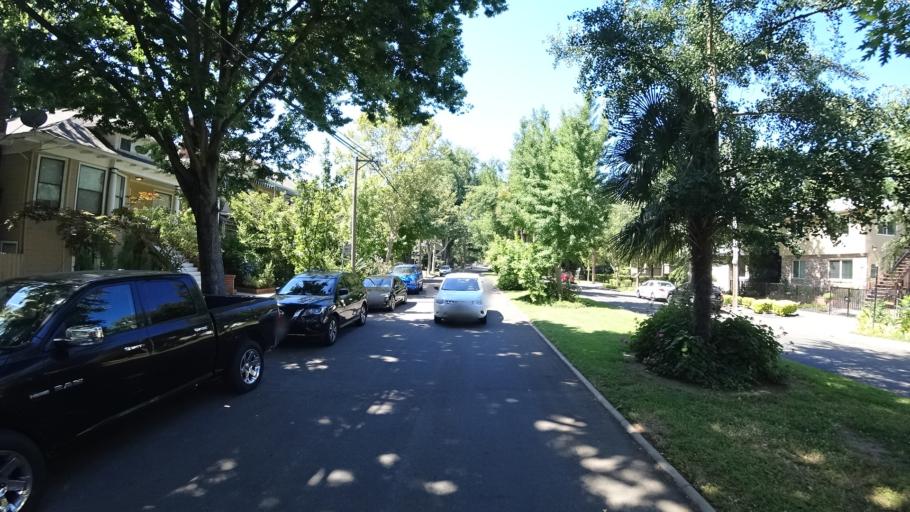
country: US
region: California
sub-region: Sacramento County
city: Sacramento
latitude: 38.5790
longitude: -121.4758
